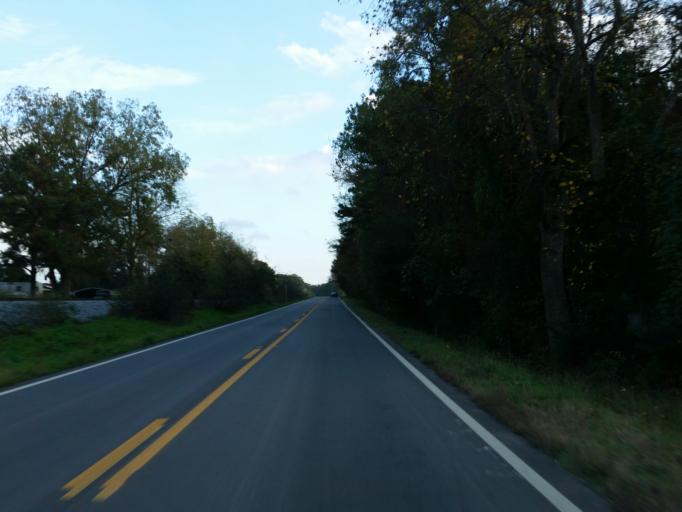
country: US
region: Georgia
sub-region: Monroe County
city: Forsyth
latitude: 32.9604
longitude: -83.8637
